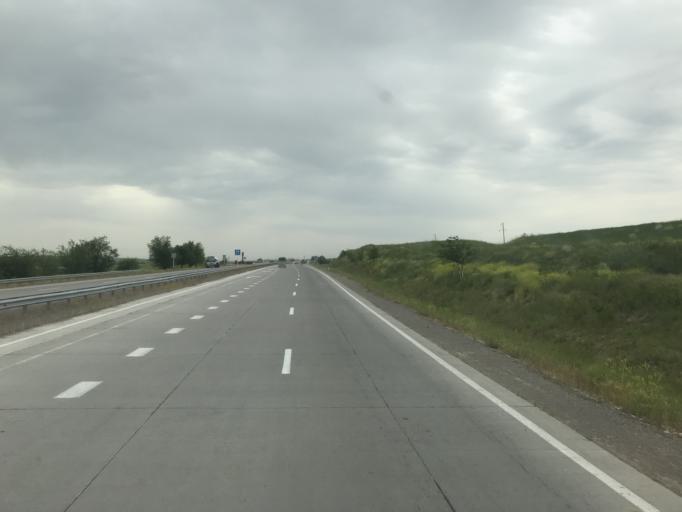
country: KZ
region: Ongtustik Qazaqstan
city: Qazyqurt
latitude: 41.8441
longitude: 69.4060
